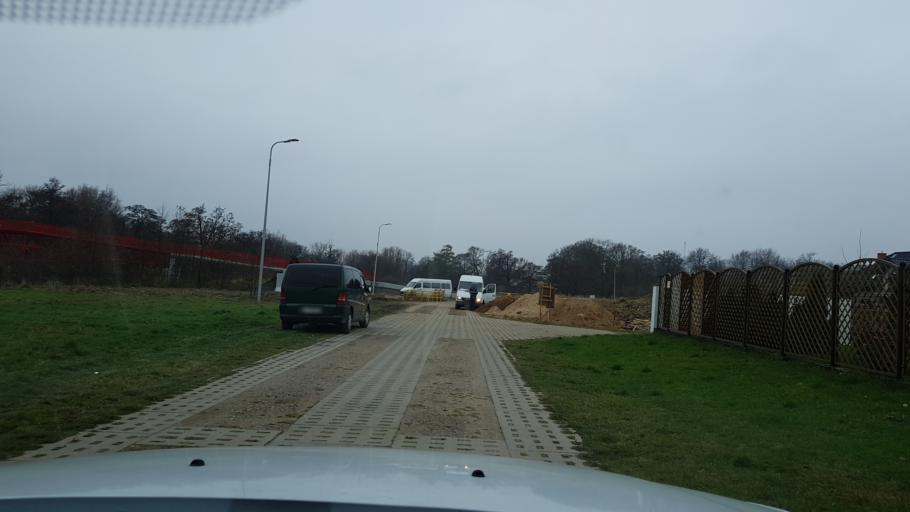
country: PL
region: West Pomeranian Voivodeship
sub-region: Powiat slawienski
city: Darlowo
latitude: 54.4155
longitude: 16.4175
